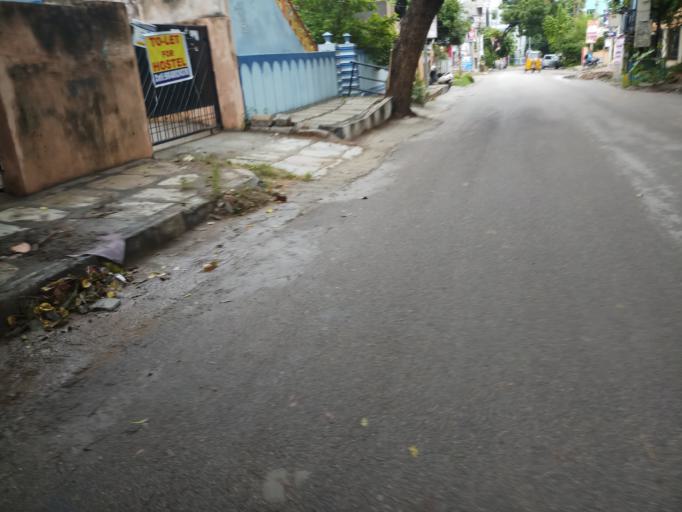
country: IN
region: Telangana
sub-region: Rangareddi
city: Gaddi Annaram
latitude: 17.3669
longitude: 78.5184
